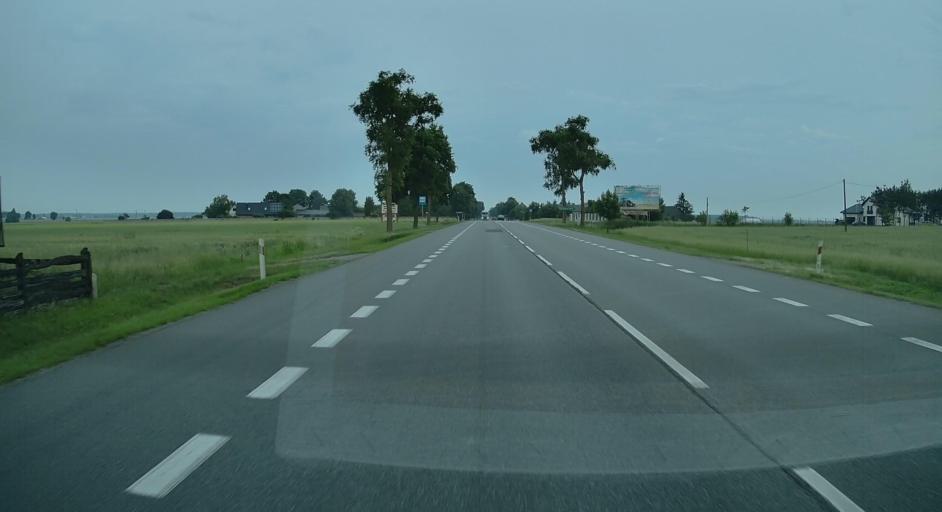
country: PL
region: Masovian Voivodeship
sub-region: Powiat siedlecki
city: Zbuczyn
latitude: 52.1162
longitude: 22.3673
